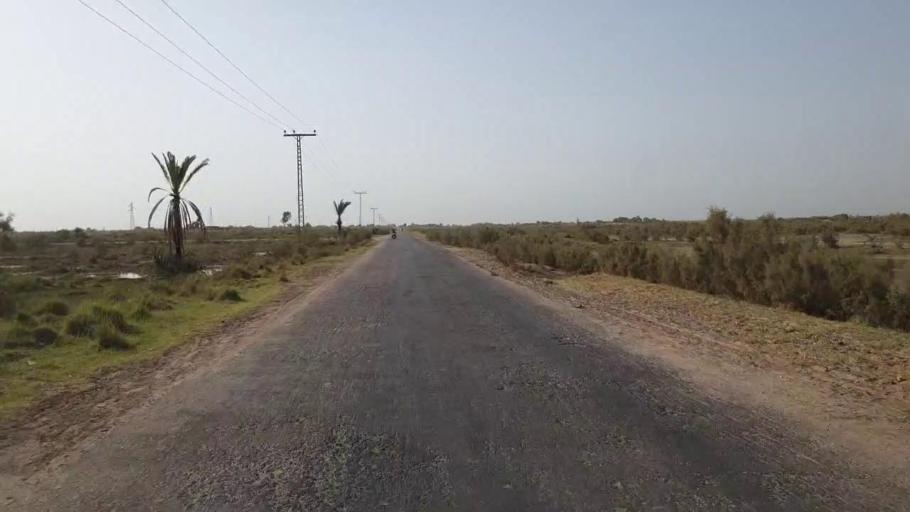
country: PK
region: Sindh
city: Khadro
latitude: 26.3472
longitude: 68.9240
